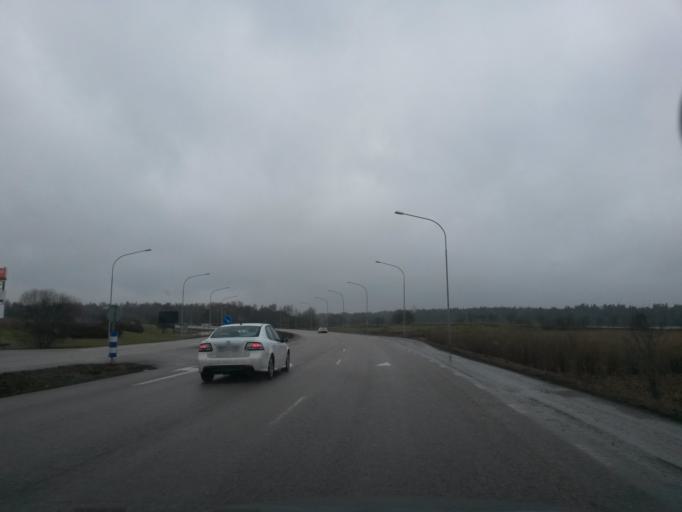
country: SE
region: Vaestra Goetaland
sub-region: Vanersborgs Kommun
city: Vanersborg
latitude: 58.3638
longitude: 12.3148
